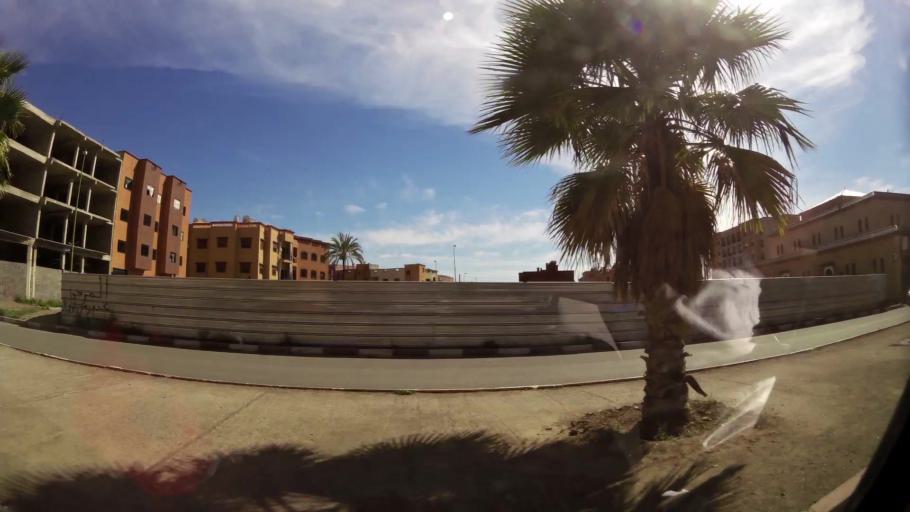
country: MA
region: Marrakech-Tensift-Al Haouz
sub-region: Marrakech
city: Marrakesh
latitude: 31.6694
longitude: -8.0274
